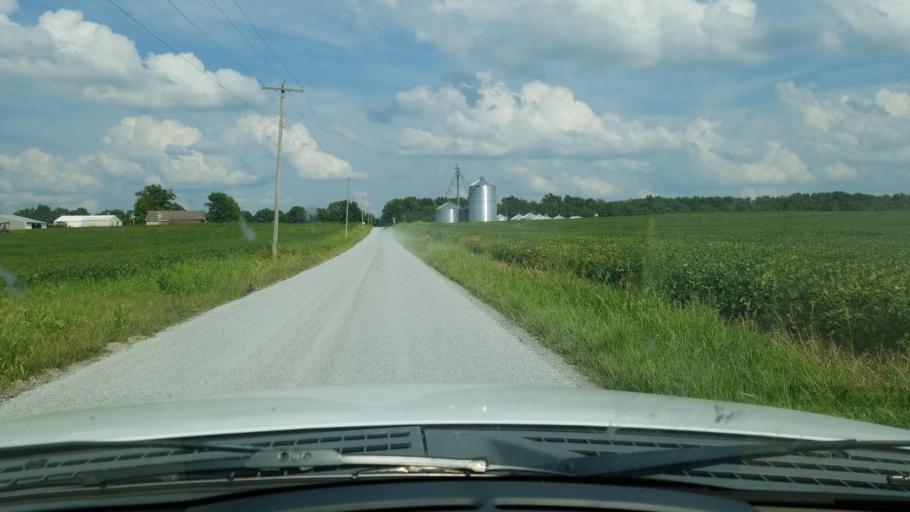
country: US
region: Illinois
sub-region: Saline County
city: Eldorado
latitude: 37.8344
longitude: -88.4471
